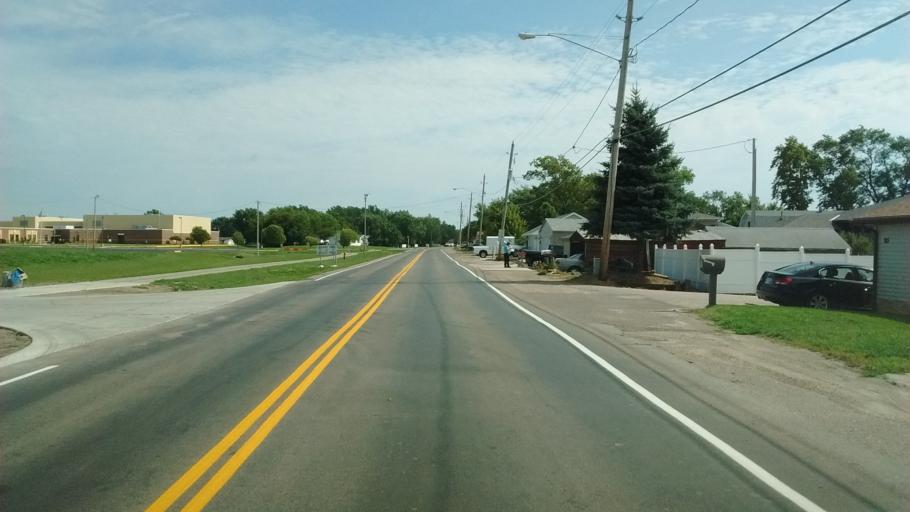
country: US
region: South Dakota
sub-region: Union County
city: North Sioux City
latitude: 42.5493
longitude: -96.5208
